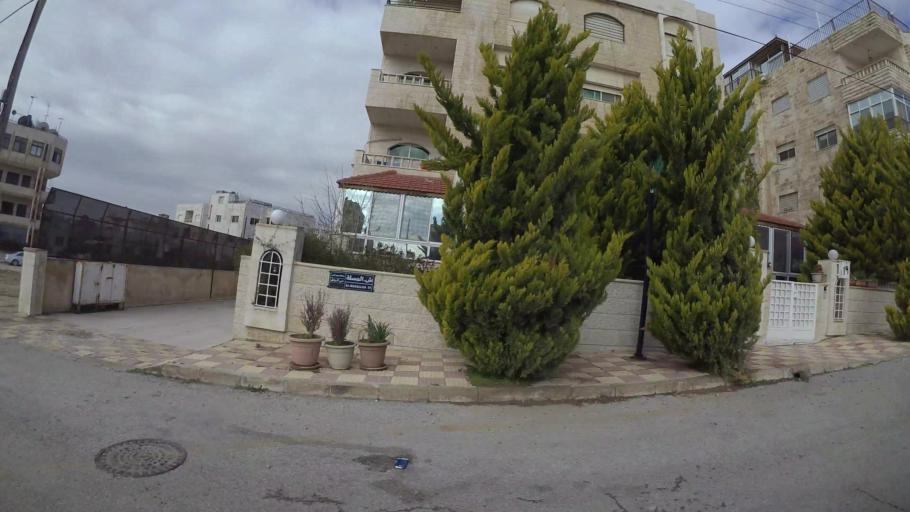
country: JO
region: Amman
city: Wadi as Sir
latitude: 31.9471
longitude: 35.8453
